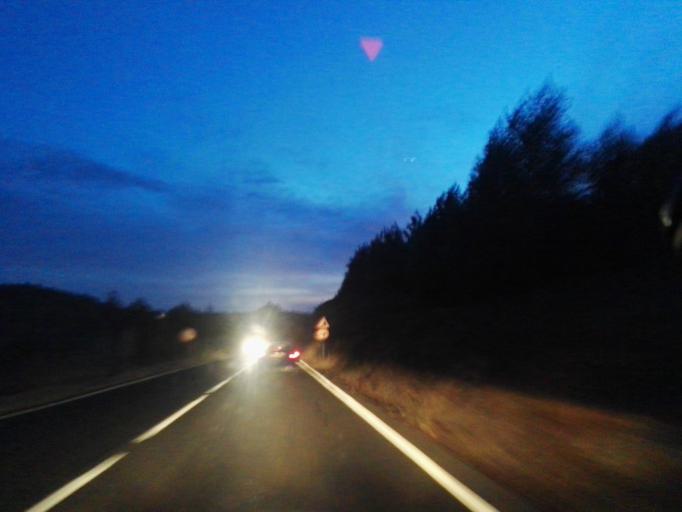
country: PT
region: Lisbon
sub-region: Cascais
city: Alcabideche
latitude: 38.7398
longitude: -9.4546
